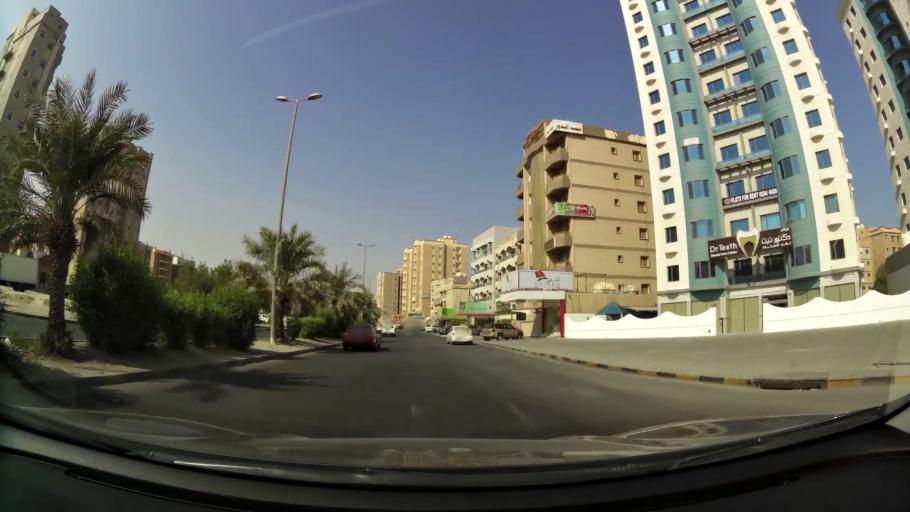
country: KW
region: Al Ahmadi
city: Al Manqaf
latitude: 29.0944
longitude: 48.1299
